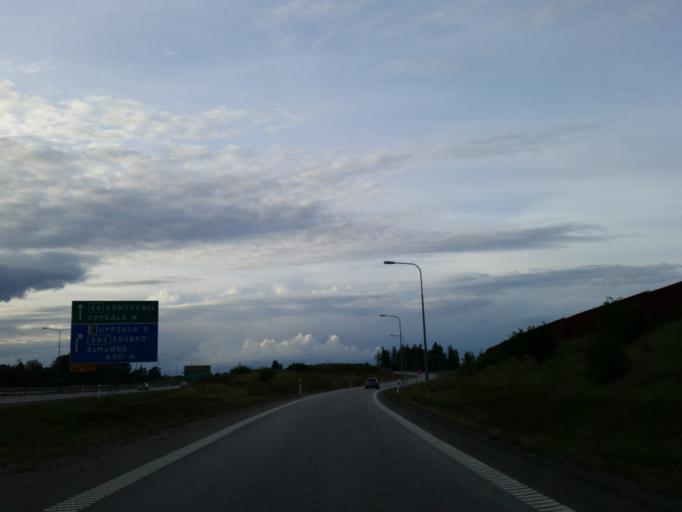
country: SE
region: Uppsala
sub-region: Uppsala Kommun
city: Saevja
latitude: 59.8316
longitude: 17.7358
